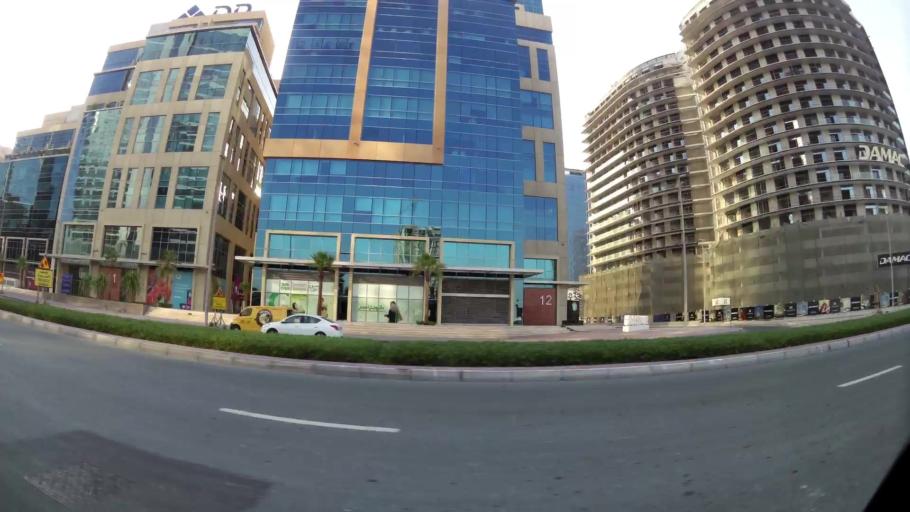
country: AE
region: Dubai
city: Dubai
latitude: 25.1855
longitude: 55.2822
